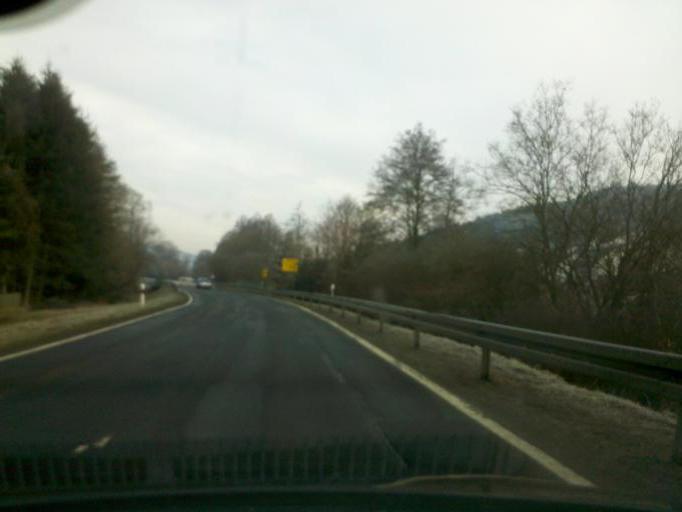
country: DE
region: Hesse
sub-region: Regierungsbezirk Giessen
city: Haiger
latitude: 50.7698
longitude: 8.2111
